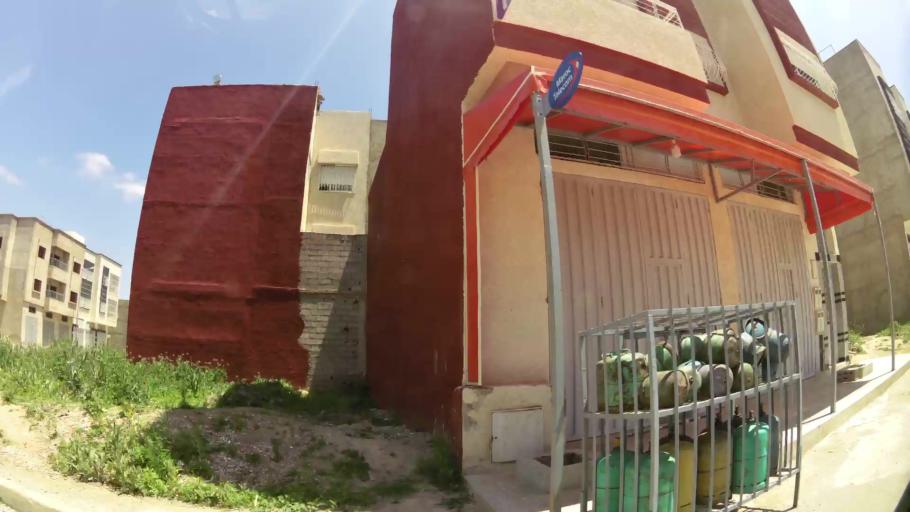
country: MA
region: Fes-Boulemane
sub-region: Fes
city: Fes
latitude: 34.0344
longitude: -5.0541
